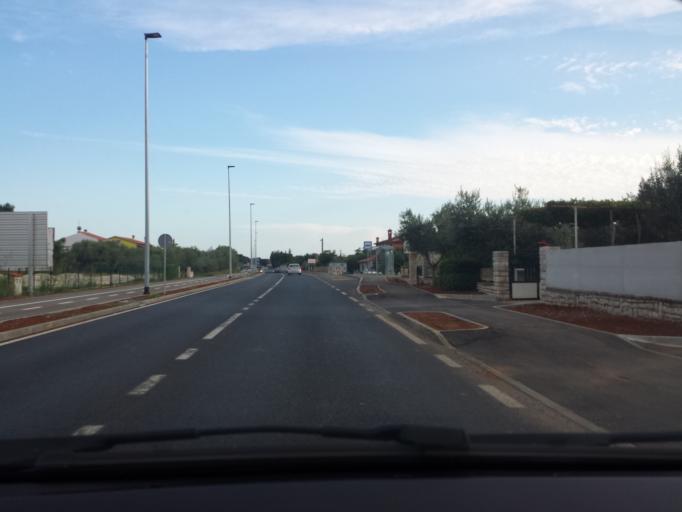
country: HR
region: Istarska
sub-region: Grad Pula
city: Pula
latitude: 44.9034
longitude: 13.8461
